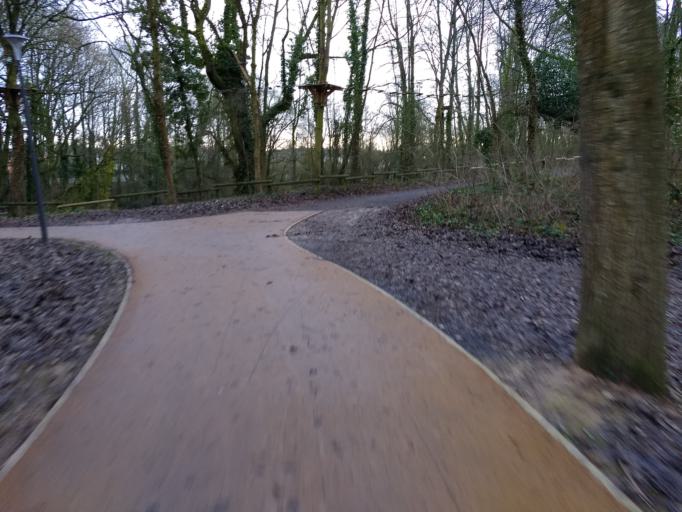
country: FR
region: Nord-Pas-de-Calais
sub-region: Departement du Pas-de-Calais
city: Achicourt
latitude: 50.2830
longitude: 2.7632
